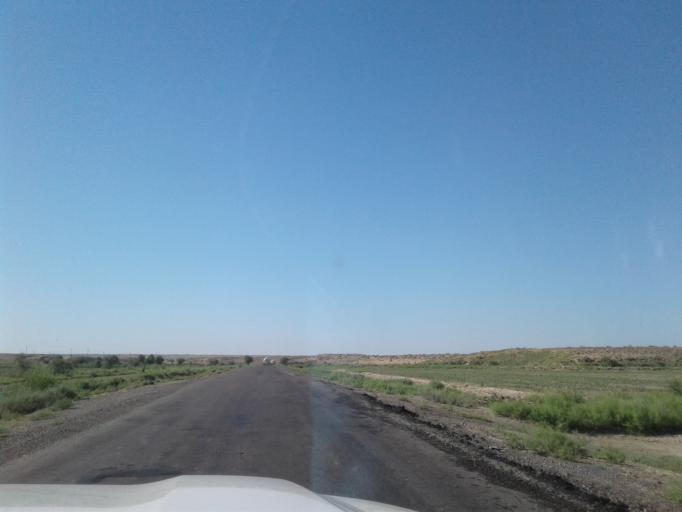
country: TM
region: Mary
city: Yoloeten
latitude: 36.7785
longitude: 62.4771
